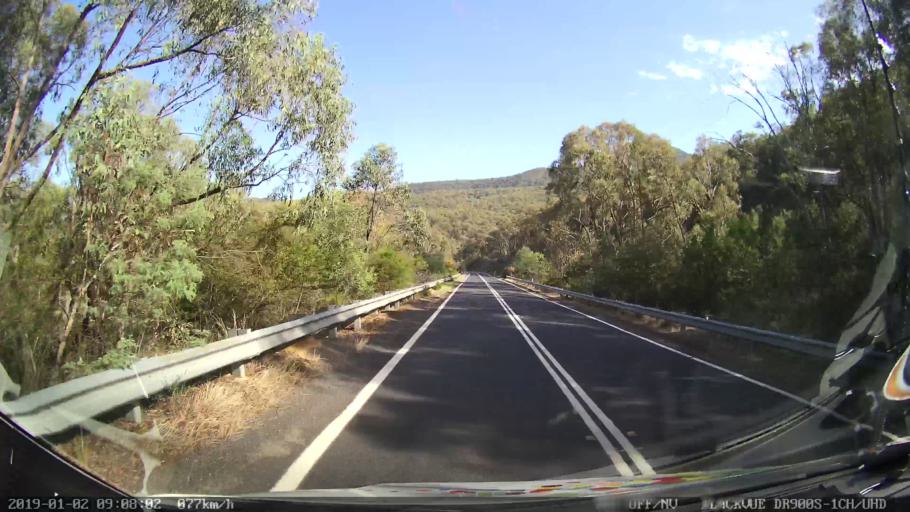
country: AU
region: New South Wales
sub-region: Tumut Shire
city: Tumut
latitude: -35.5344
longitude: 148.2949
